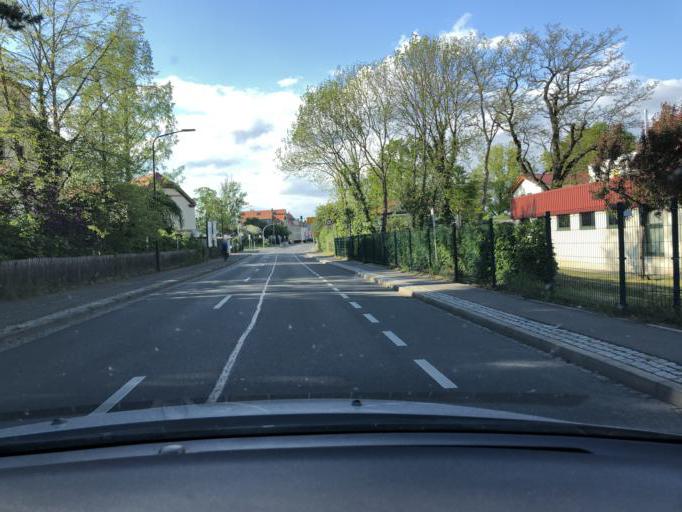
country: DE
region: Saxony
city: Markkleeberg
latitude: 51.2610
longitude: 12.3782
